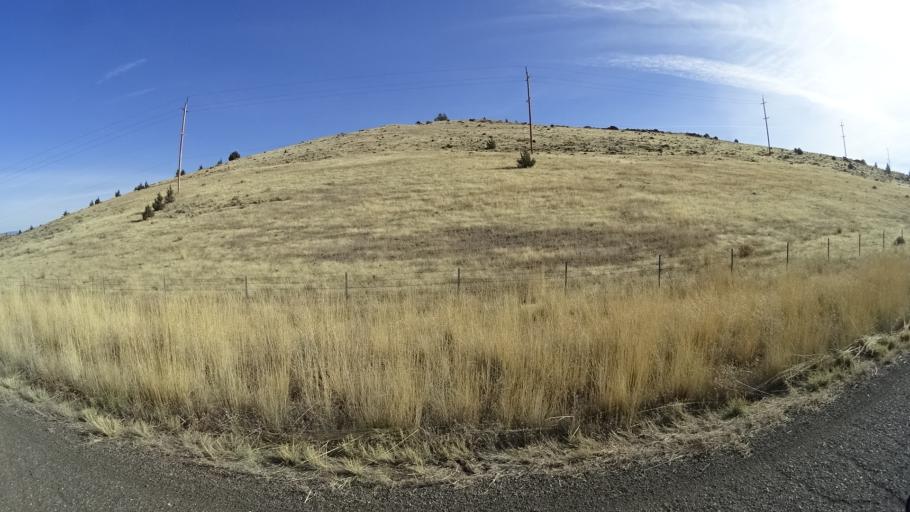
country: US
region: California
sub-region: Siskiyou County
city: Weed
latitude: 41.5182
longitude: -122.4729
